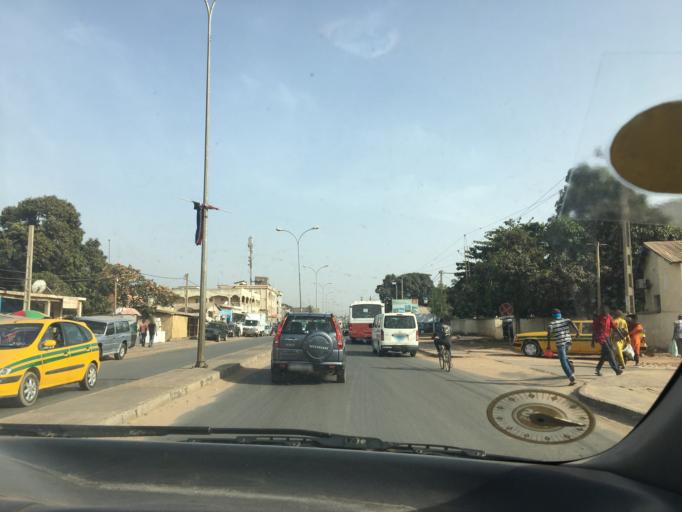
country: GM
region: Western
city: Abuko
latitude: 13.4348
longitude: -16.6762
